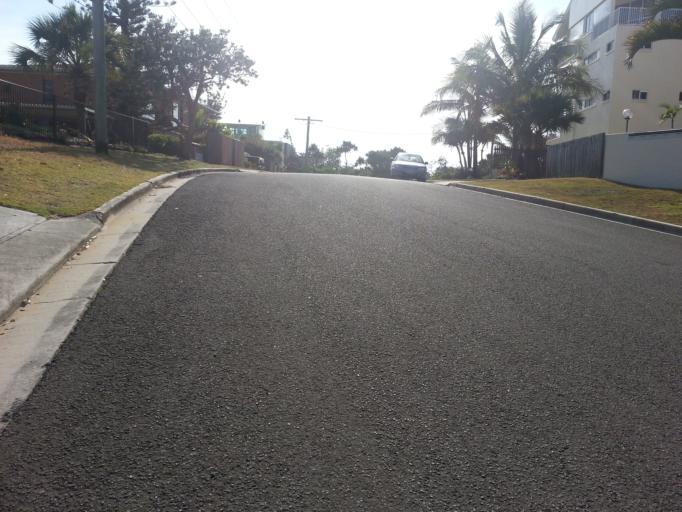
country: AU
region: Queensland
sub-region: Sunshine Coast
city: Peregian Springs
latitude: -26.4948
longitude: 153.0943
